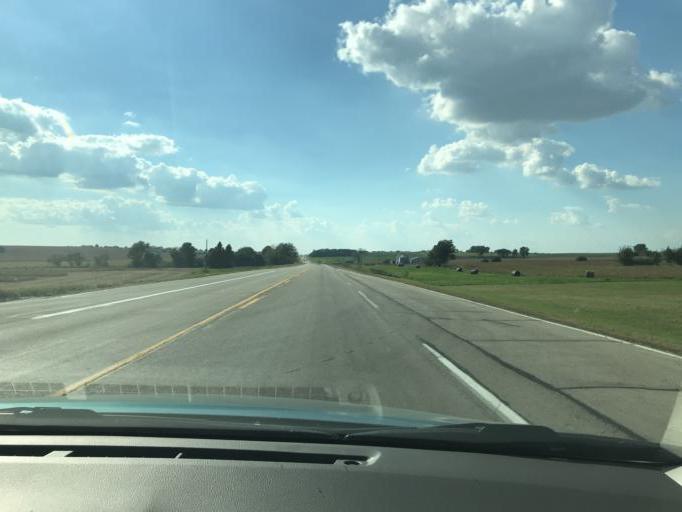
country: US
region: Wisconsin
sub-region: Green County
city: Brodhead
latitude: 42.5883
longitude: -89.4259
